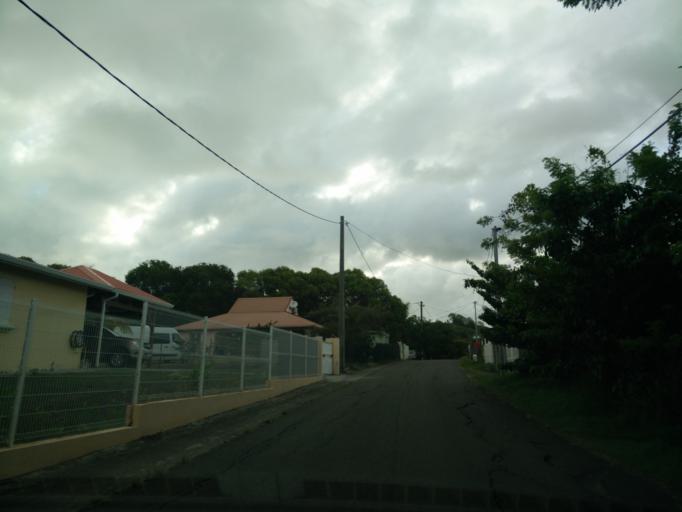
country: MQ
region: Martinique
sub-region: Martinique
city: Le Marin
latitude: 14.4482
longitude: -60.8386
